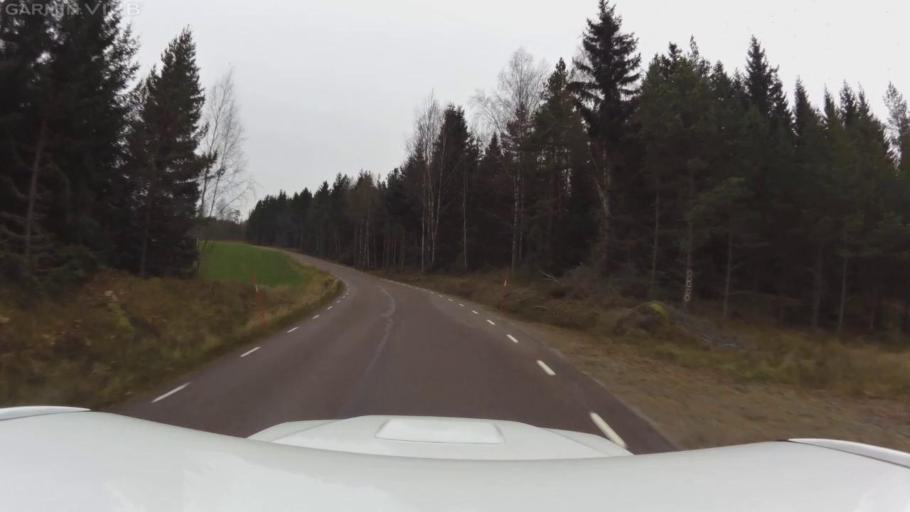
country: SE
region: OEstergoetland
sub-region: Mjolby Kommun
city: Mantorp
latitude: 58.1614
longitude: 15.3926
